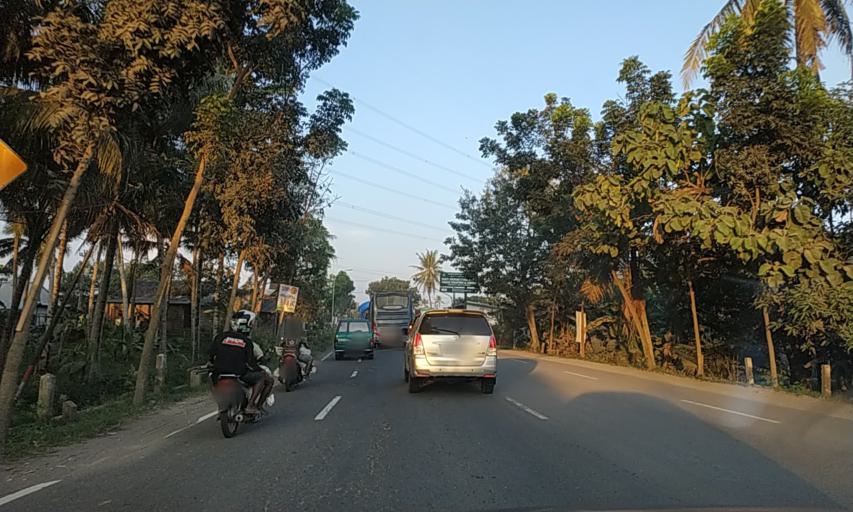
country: ID
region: Daerah Istimewa Yogyakarta
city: Srandakan
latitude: -7.8868
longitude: 110.0562
